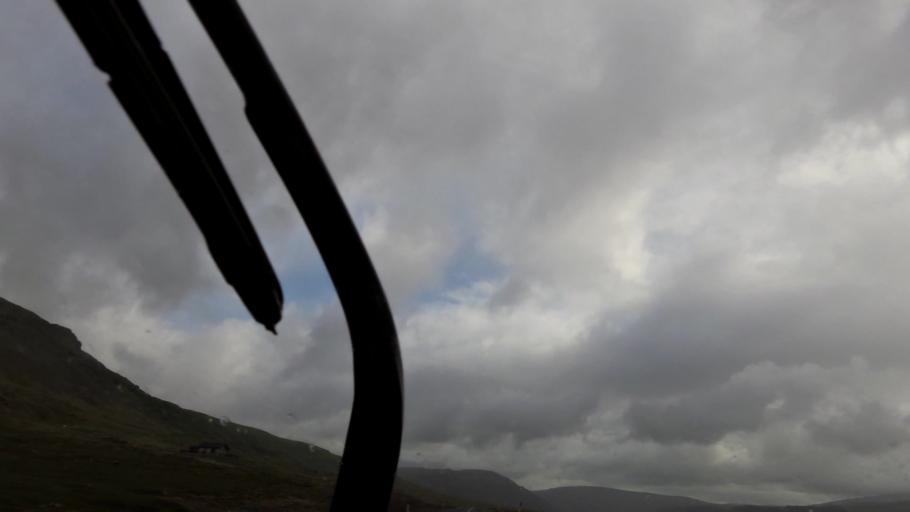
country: IS
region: Westfjords
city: Isafjoerdur
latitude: 65.5499
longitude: -23.1998
